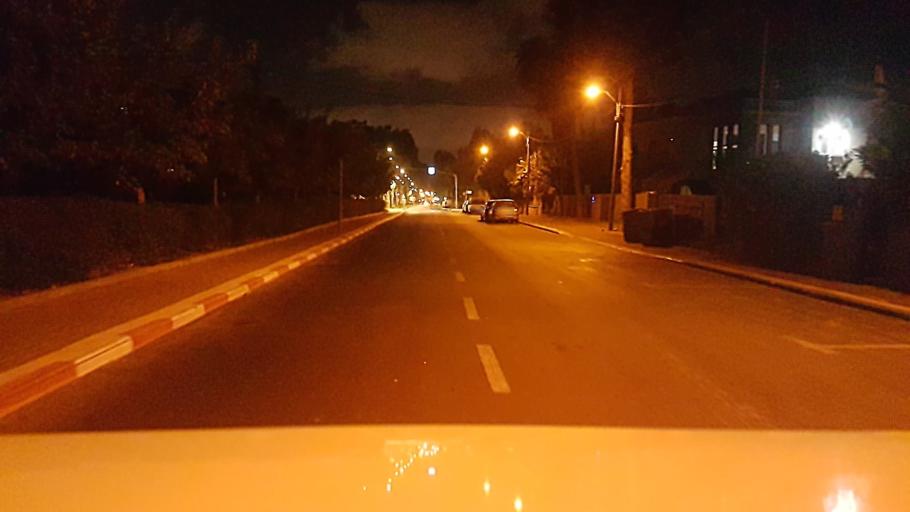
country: IL
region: Central District
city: Nehalim
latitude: 32.0772
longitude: 34.9154
